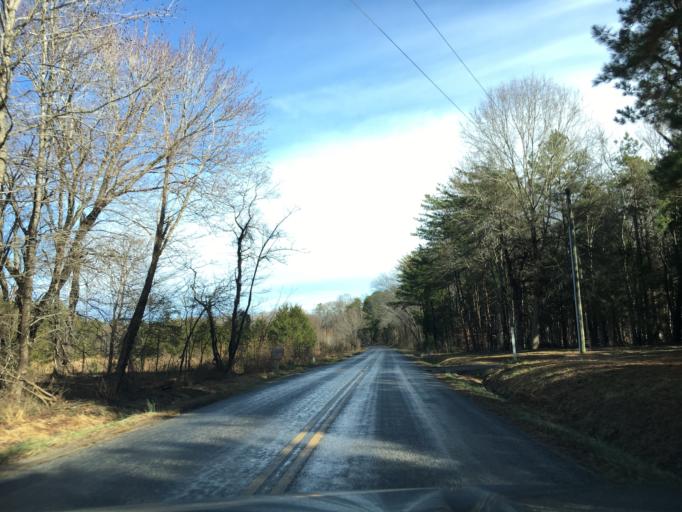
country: US
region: Virginia
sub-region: Cumberland County
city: Cumberland
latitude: 37.3476
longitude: -78.1580
